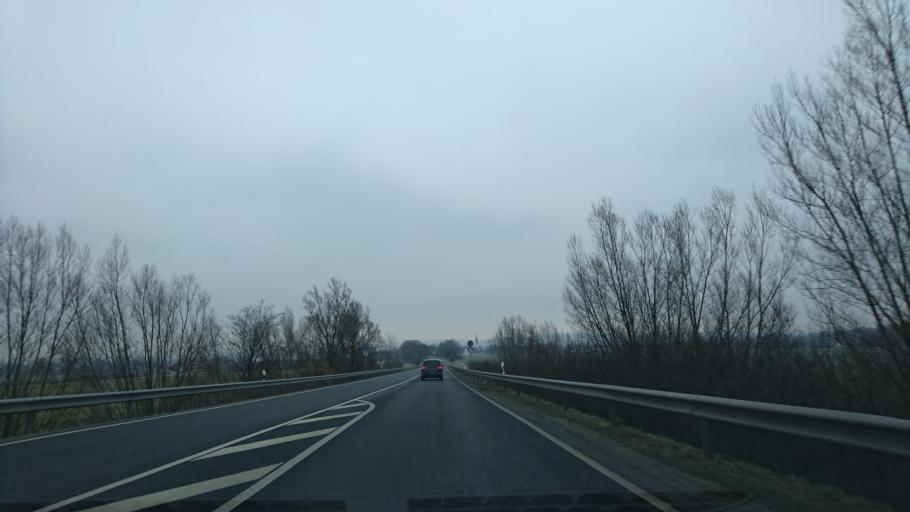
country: AT
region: Upper Austria
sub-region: Politischer Bezirk Scharding
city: Scharding
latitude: 48.4366
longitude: 13.3802
